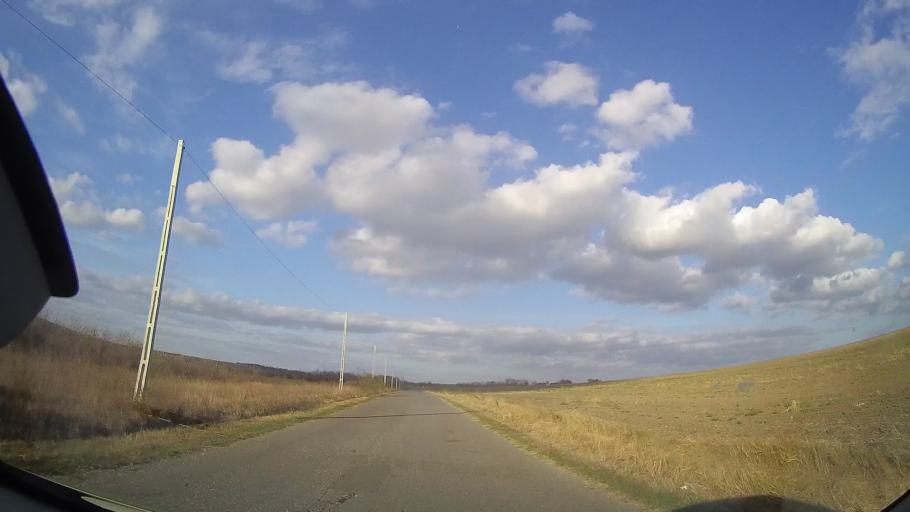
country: RO
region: Constanta
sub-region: Comuna Cerchezu
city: Cerchezu
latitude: 43.8480
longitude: 28.0993
